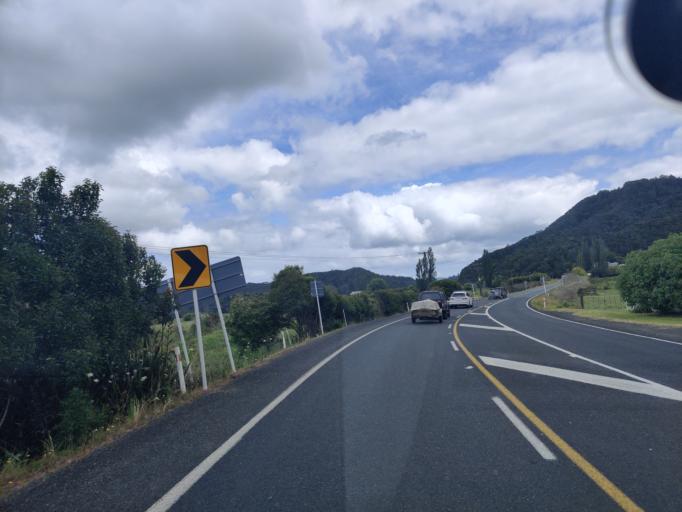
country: NZ
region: Northland
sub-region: Far North District
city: Kerikeri
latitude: -35.0981
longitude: 173.7740
